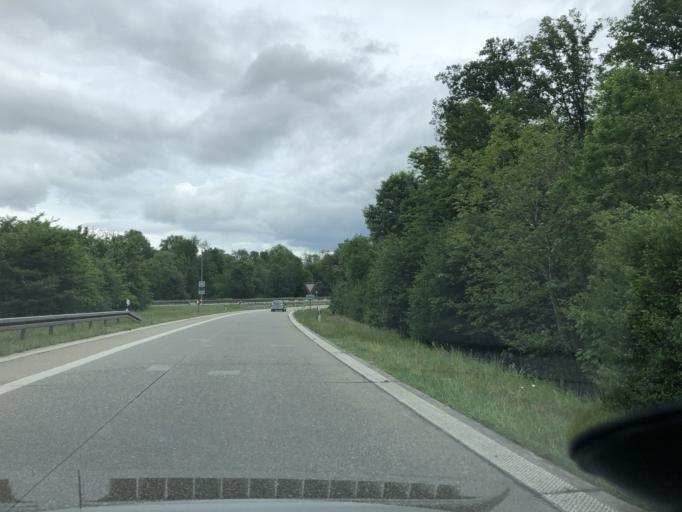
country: DE
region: Baden-Wuerttemberg
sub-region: Freiburg Region
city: Umkirch
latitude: 48.0232
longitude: 7.7866
